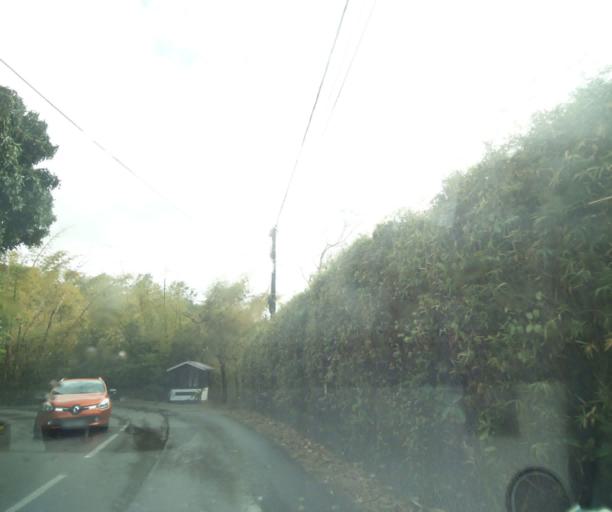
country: RE
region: Reunion
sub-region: Reunion
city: Saint-Paul
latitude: -21.0086
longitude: 55.3188
